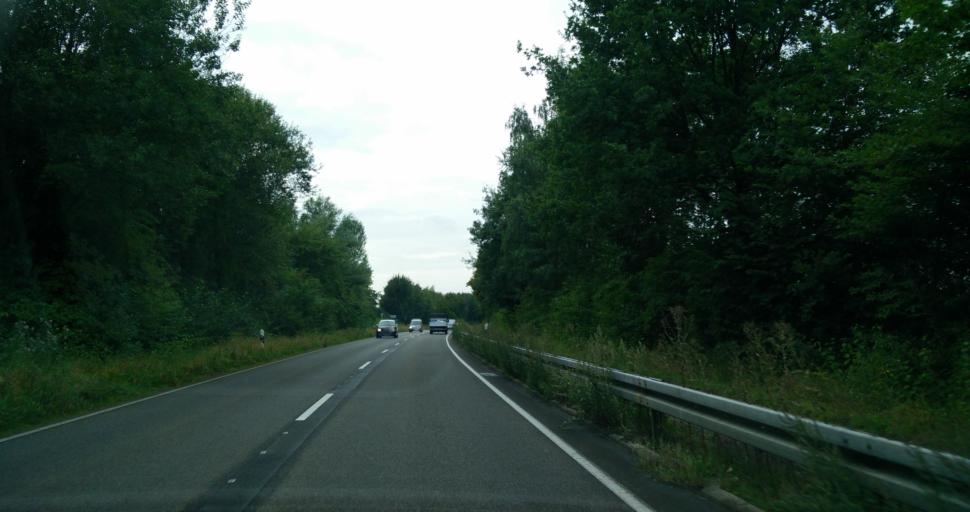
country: DE
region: North Rhine-Westphalia
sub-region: Regierungsbezirk Dusseldorf
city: Erkrath
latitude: 51.2689
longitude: 6.9234
